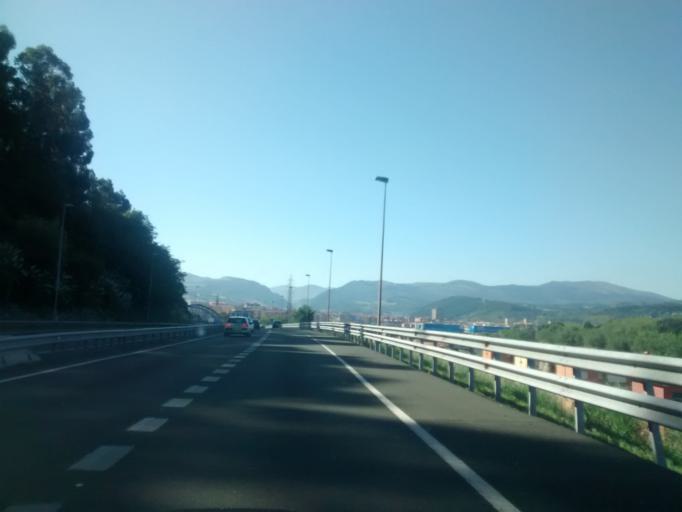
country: ES
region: Cantabria
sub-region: Provincia de Cantabria
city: Torrelavega
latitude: 43.3630
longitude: -4.0436
